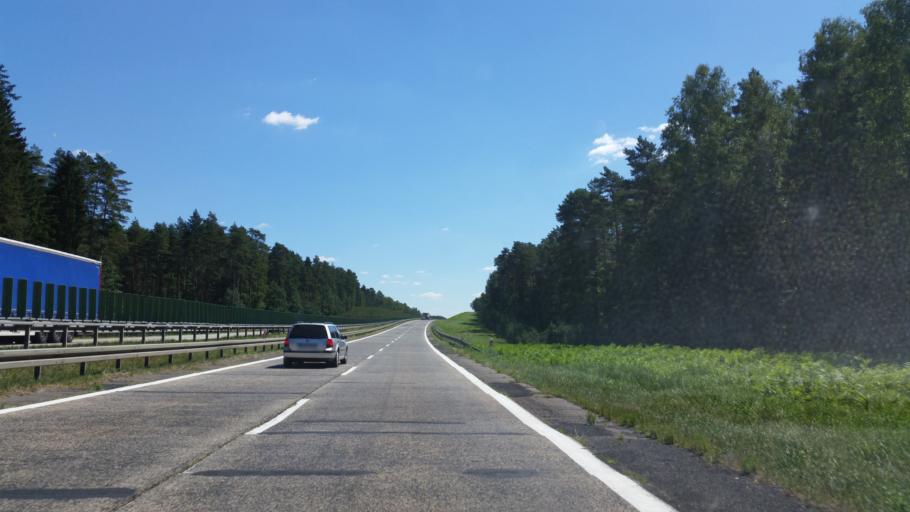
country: PL
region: Lubusz
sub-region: Powiat zaganski
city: Malomice
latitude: 51.4142
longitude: 15.4911
